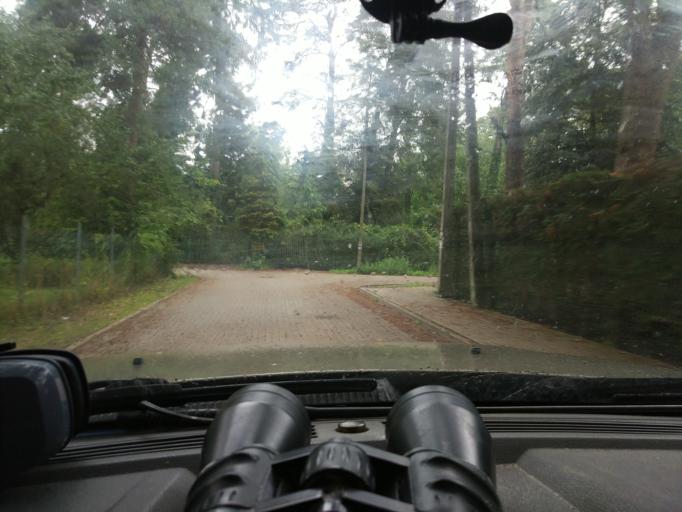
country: PL
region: Masovian Voivodeship
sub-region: Powiat grodziski
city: Podkowa Lesna
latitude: 52.1257
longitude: 20.7372
